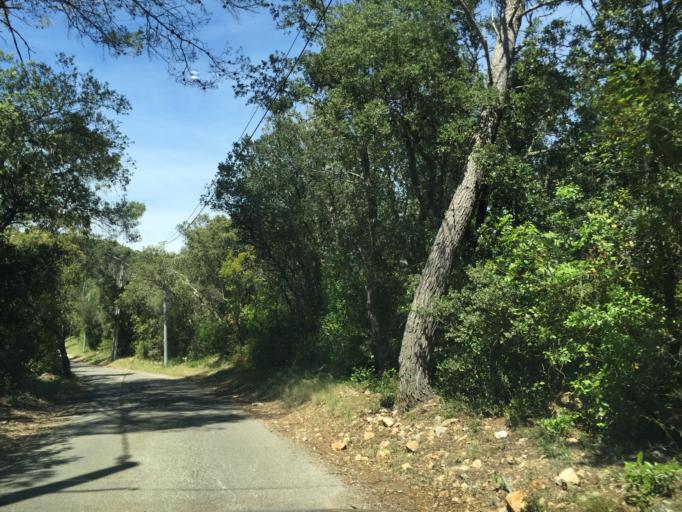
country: FR
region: Provence-Alpes-Cote d'Azur
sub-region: Departement du Var
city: Lorgues
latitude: 43.4754
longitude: 6.3690
